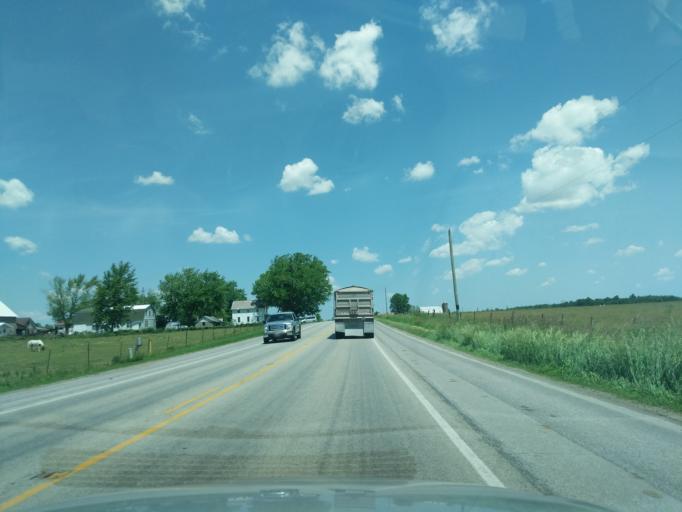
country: US
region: Indiana
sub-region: LaGrange County
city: Topeka
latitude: 41.6355
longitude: -85.5798
